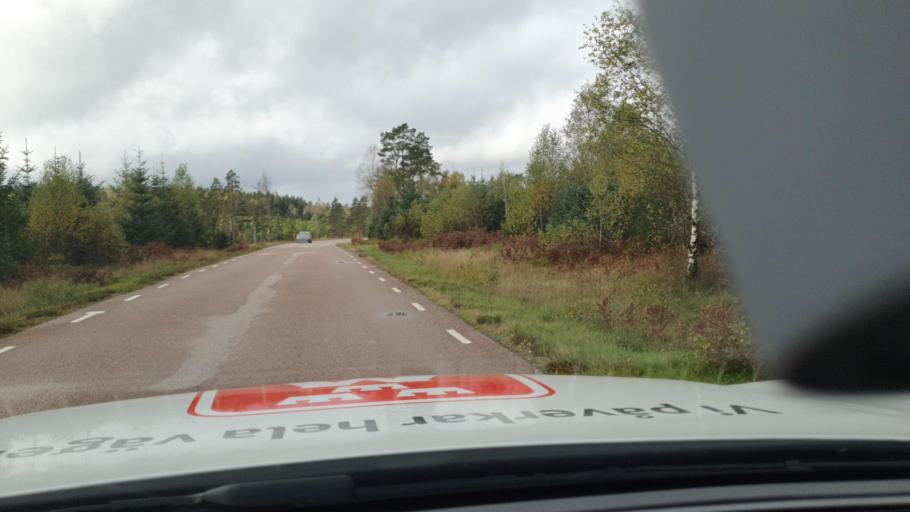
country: SE
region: Halland
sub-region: Hylte Kommun
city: Torup
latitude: 57.0021
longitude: 12.9205
